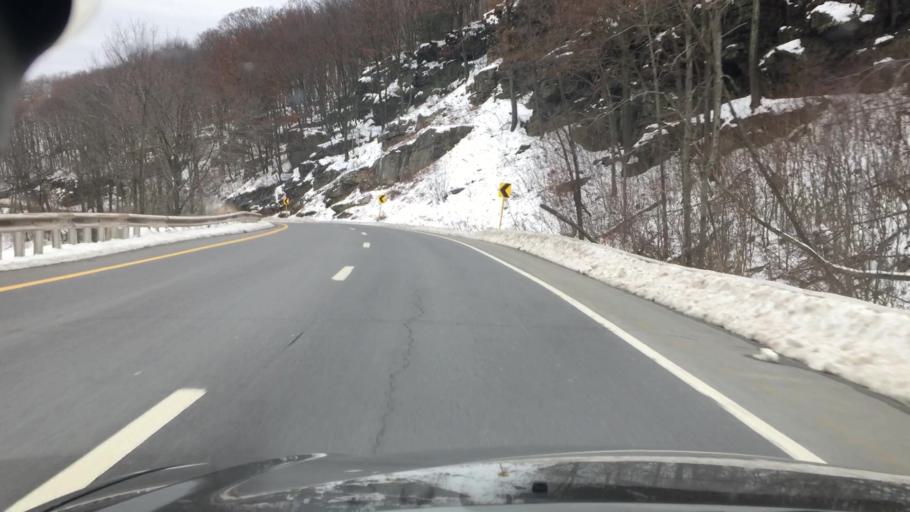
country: US
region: Pennsylvania
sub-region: Luzerne County
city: Mountain Top
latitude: 41.1840
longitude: -75.8899
